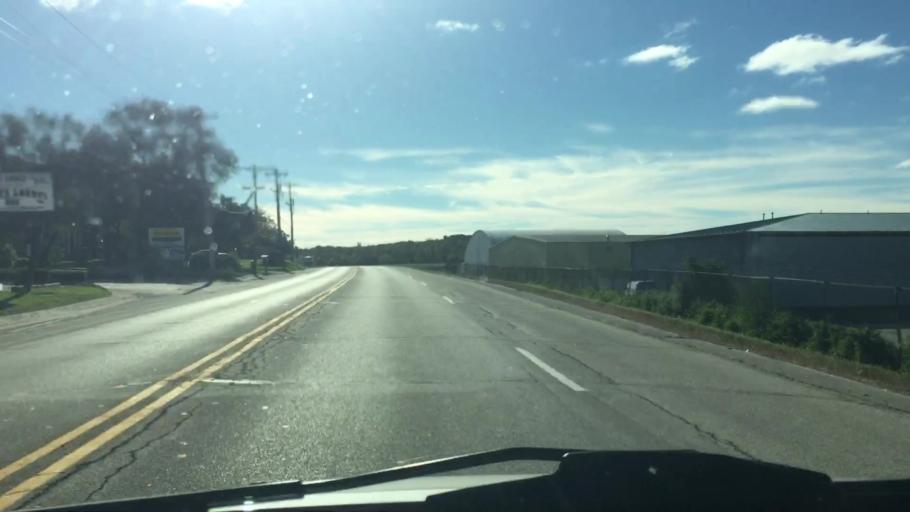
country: US
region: Wisconsin
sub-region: Waukesha County
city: Waukesha
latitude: 43.0438
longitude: -88.2307
